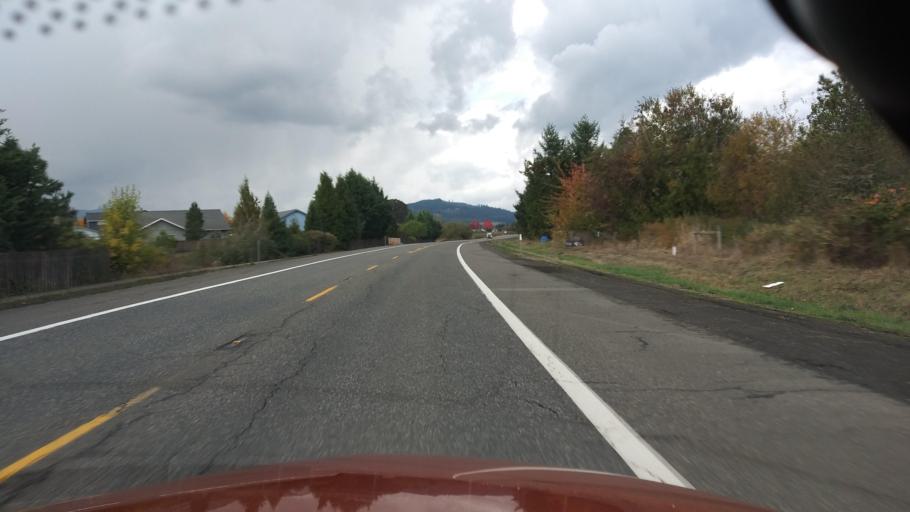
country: US
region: Oregon
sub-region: Washington County
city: Forest Grove
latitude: 45.5312
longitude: -123.0991
